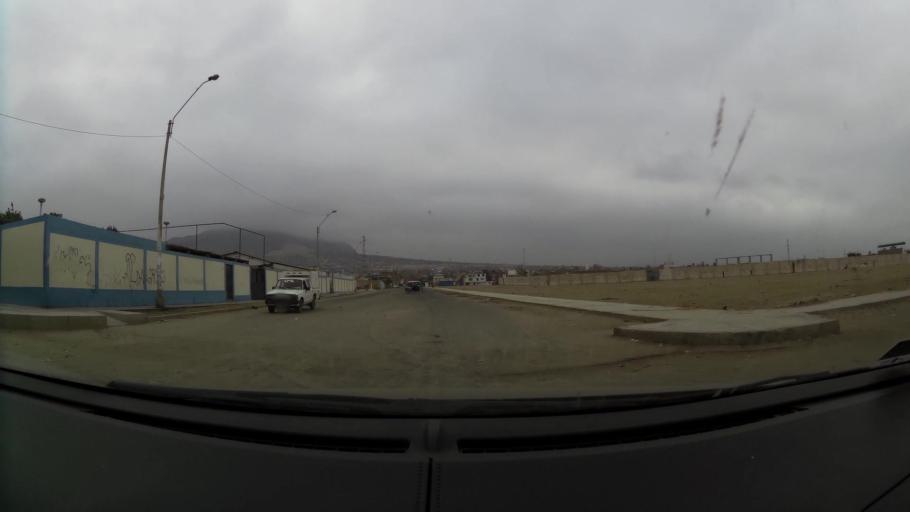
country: PE
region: La Libertad
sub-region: Provincia de Trujillo
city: La Esperanza
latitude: -8.0762
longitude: -79.0552
